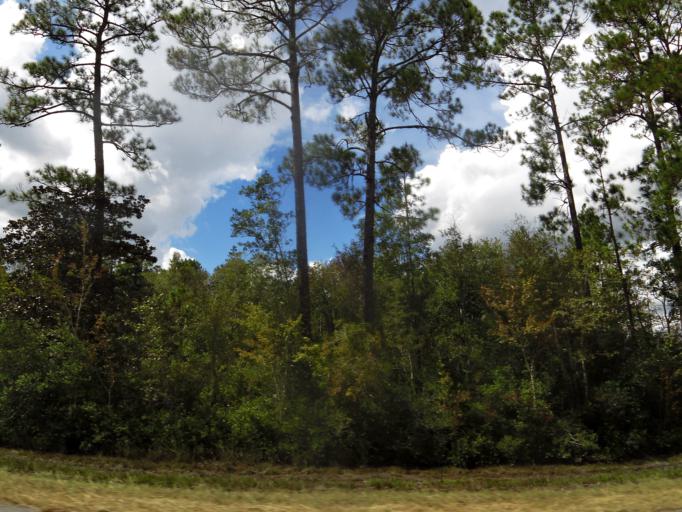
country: US
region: Georgia
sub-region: Brantley County
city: Nahunta
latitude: 31.1439
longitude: -81.9928
